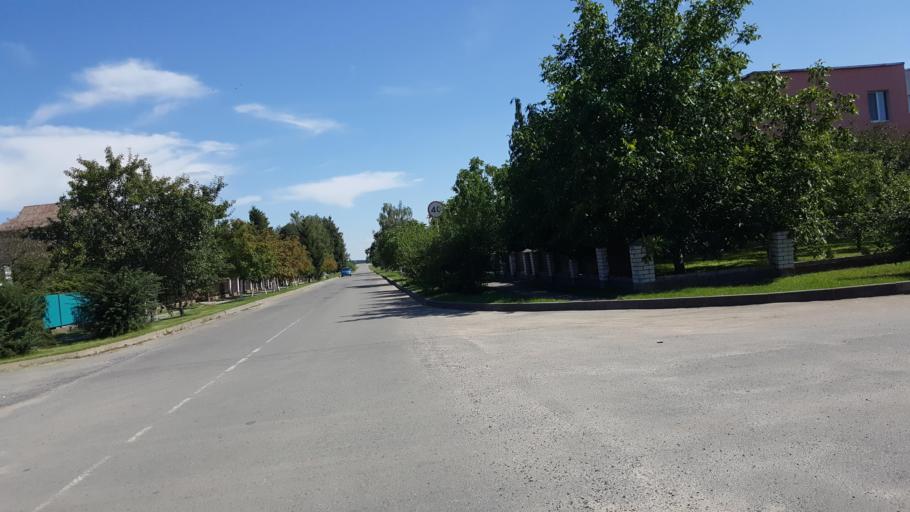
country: BY
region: Brest
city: Charnawchytsy
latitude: 52.2643
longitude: 23.5915
